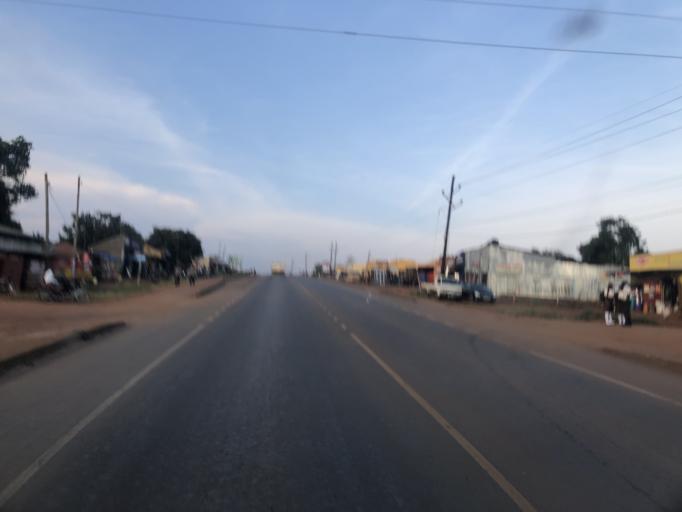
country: UG
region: Central Region
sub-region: Mpigi District
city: Mpigi
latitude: 0.2061
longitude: 32.3133
